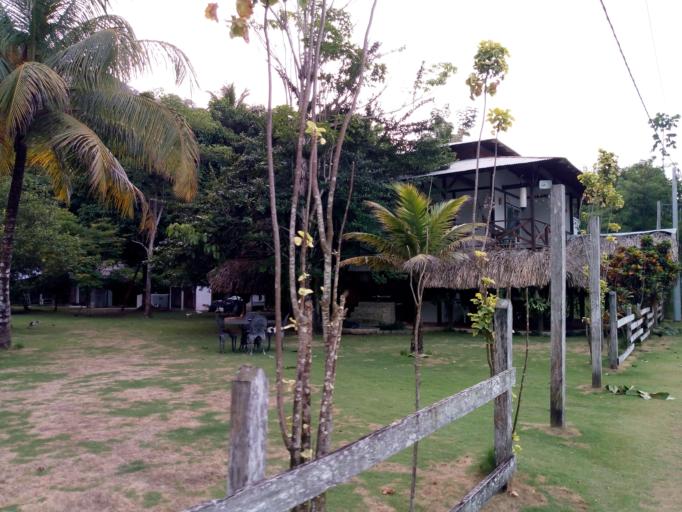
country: PA
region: Guna Yala
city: Puerto Obaldia
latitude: 8.6574
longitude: -77.3659
